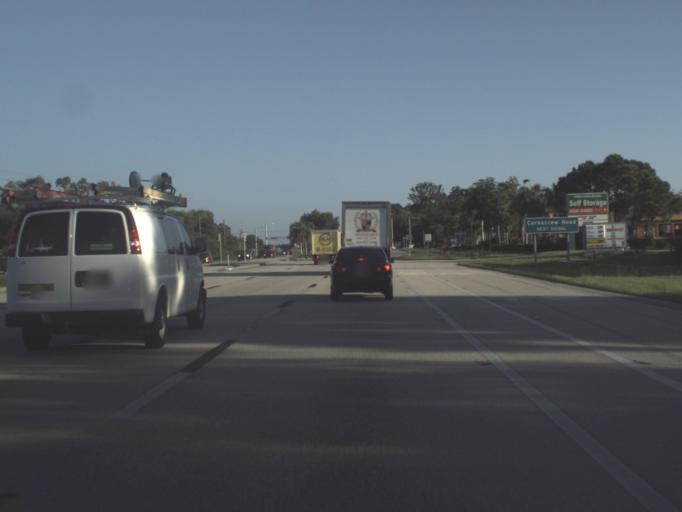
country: US
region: Florida
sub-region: Lee County
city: Estero
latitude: 26.4276
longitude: -81.8108
